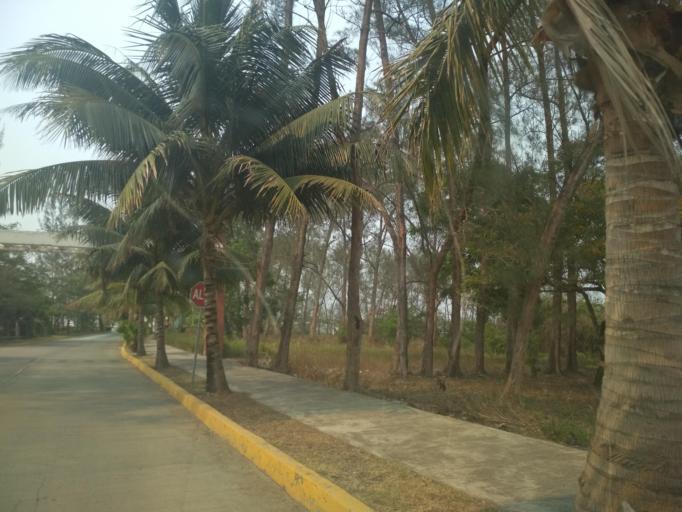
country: MX
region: Veracruz
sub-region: Veracruz
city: Las Amapolas
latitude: 19.1556
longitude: -96.2215
